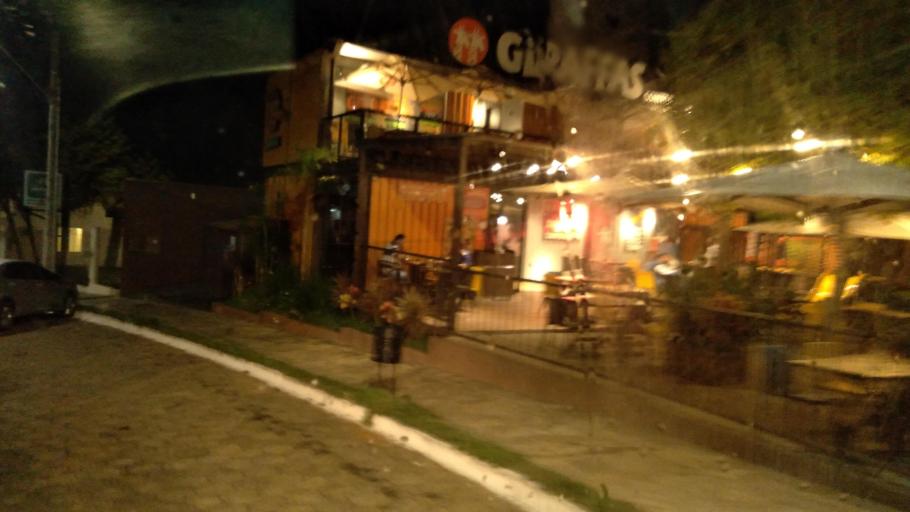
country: BR
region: Goias
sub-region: Mineiros
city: Mineiros
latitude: -17.5644
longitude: -52.5562
